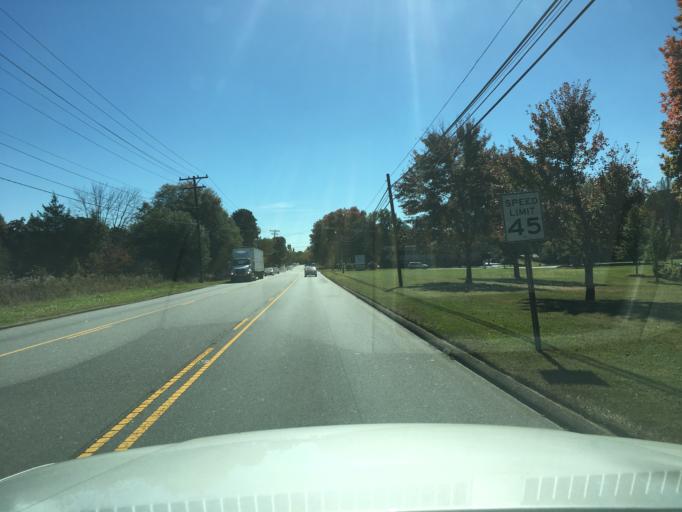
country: US
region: North Carolina
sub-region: Catawba County
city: Conover
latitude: 35.7142
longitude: -81.2652
